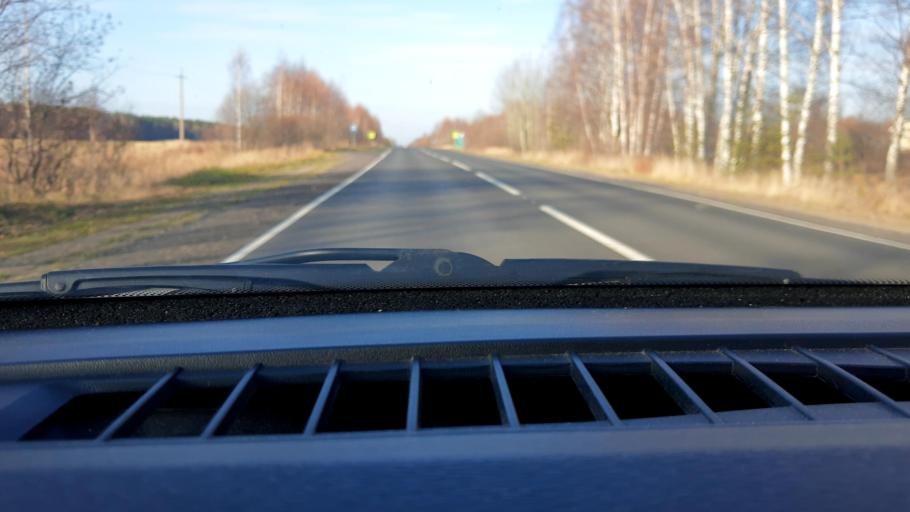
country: RU
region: Nizjnij Novgorod
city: Novaya Balakhna
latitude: 56.5902
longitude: 43.6625
